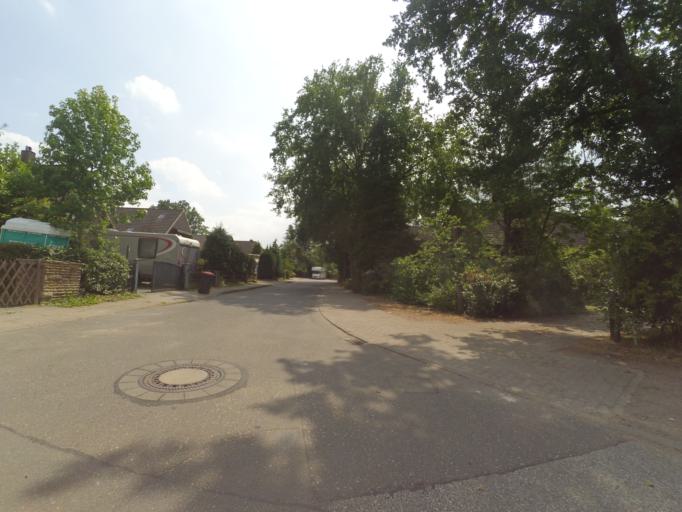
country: DE
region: Hamburg
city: Eidelstedt
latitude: 53.6319
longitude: 9.9364
